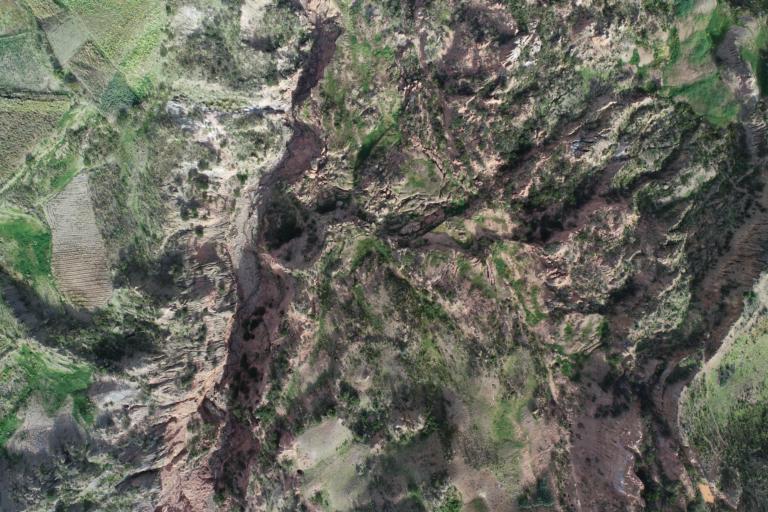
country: BO
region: La Paz
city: La Paz
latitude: -16.5536
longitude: -67.9929
